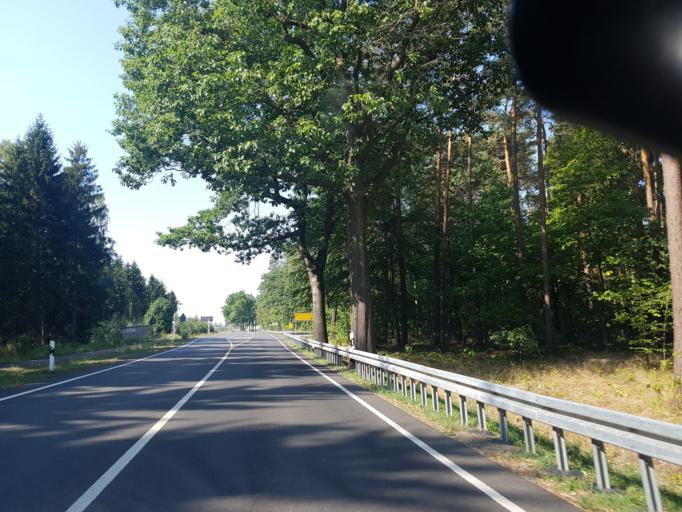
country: DE
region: Brandenburg
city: Wiesenburg
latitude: 52.1253
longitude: 12.4890
